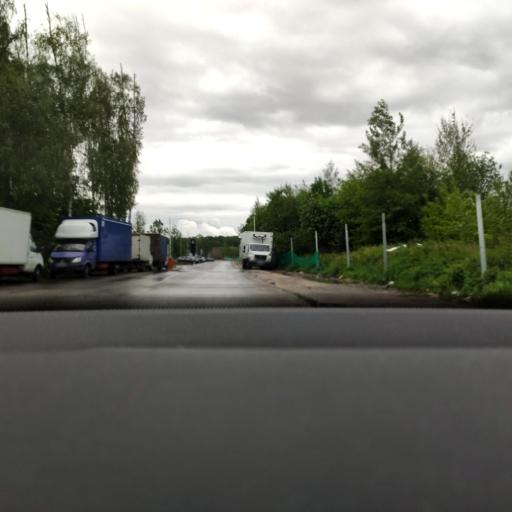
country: RU
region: Moscow
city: Lianozovo
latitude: 55.9165
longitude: 37.5875
